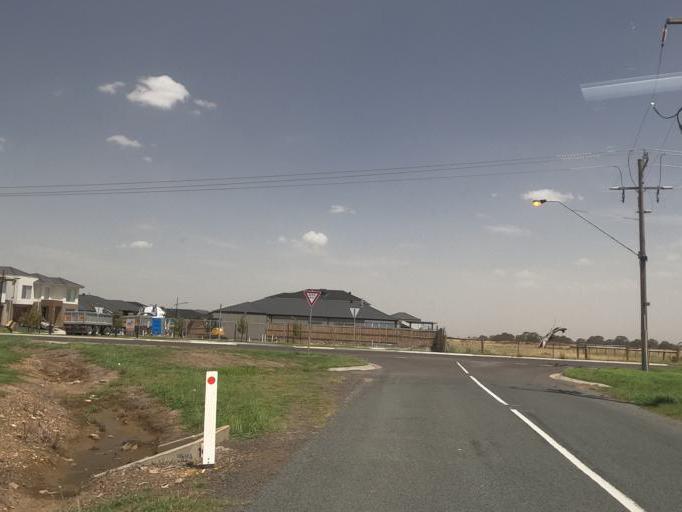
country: AU
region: Victoria
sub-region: Hume
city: Craigieburn
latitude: -37.5632
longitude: 144.8910
